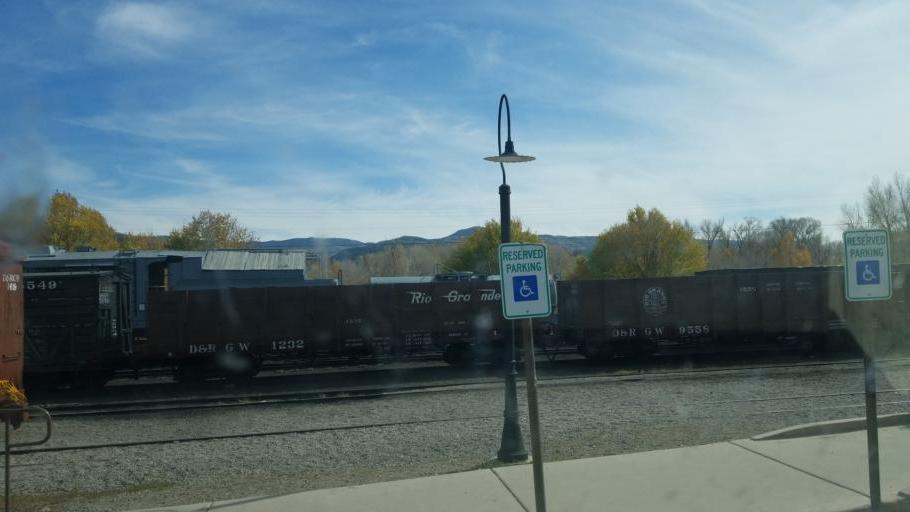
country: US
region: New Mexico
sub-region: Rio Arriba County
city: Chama
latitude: 36.9021
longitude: -106.5788
